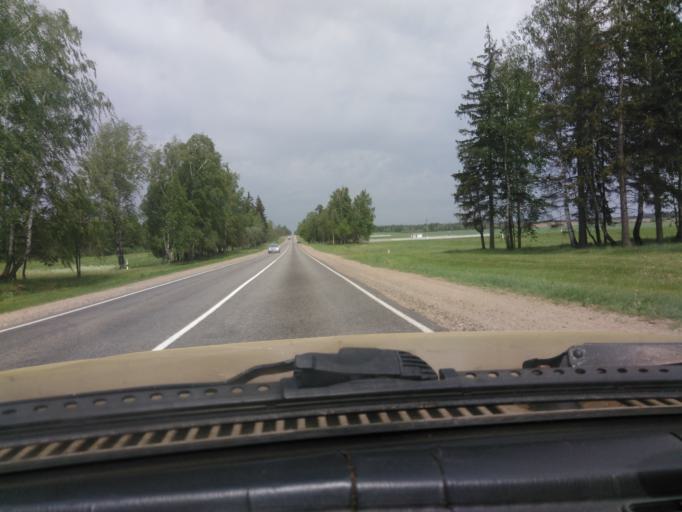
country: BY
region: Mogilev
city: Palykavichy Pyershyya
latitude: 53.9958
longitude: 30.3192
